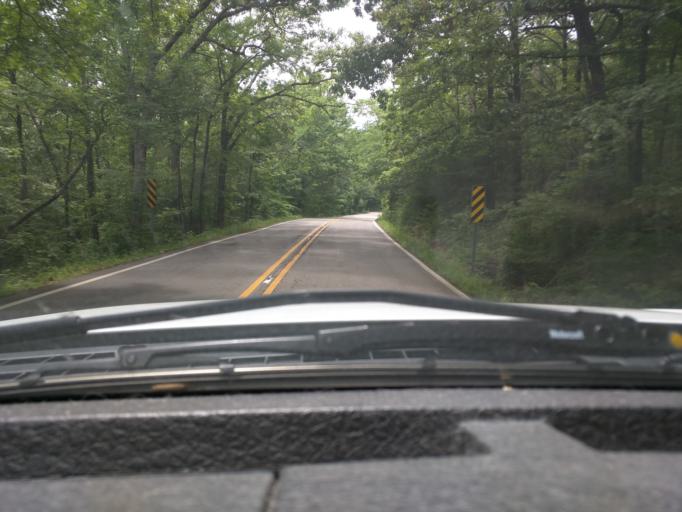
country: US
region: Arkansas
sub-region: Franklin County
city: Ozark
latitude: 35.6951
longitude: -93.8032
